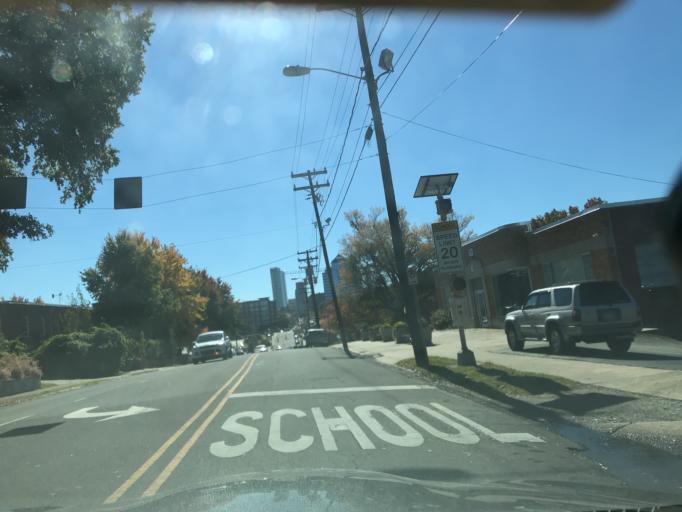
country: US
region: North Carolina
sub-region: Durham County
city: Durham
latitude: 36.0053
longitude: -78.9015
